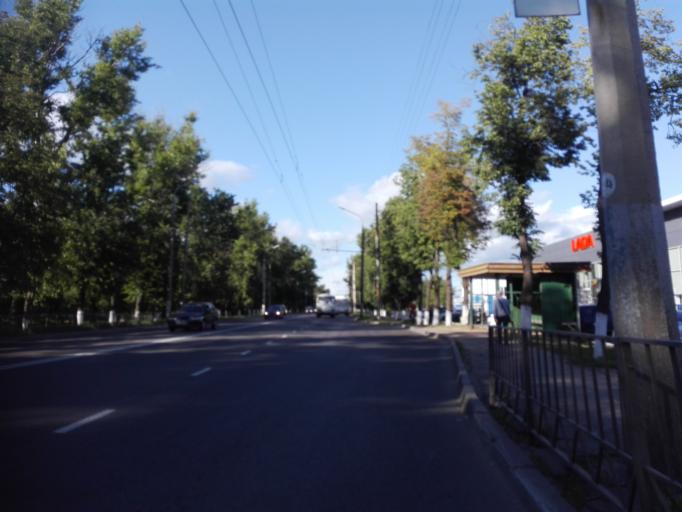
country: RU
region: Orjol
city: Orel
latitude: 53.0053
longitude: 36.1456
